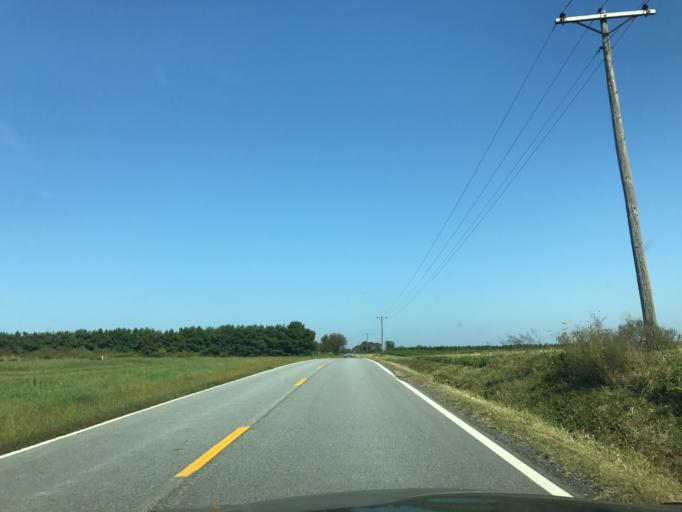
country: US
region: Maryland
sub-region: Queen Anne's County
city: Kingstown
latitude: 39.2930
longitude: -75.9294
